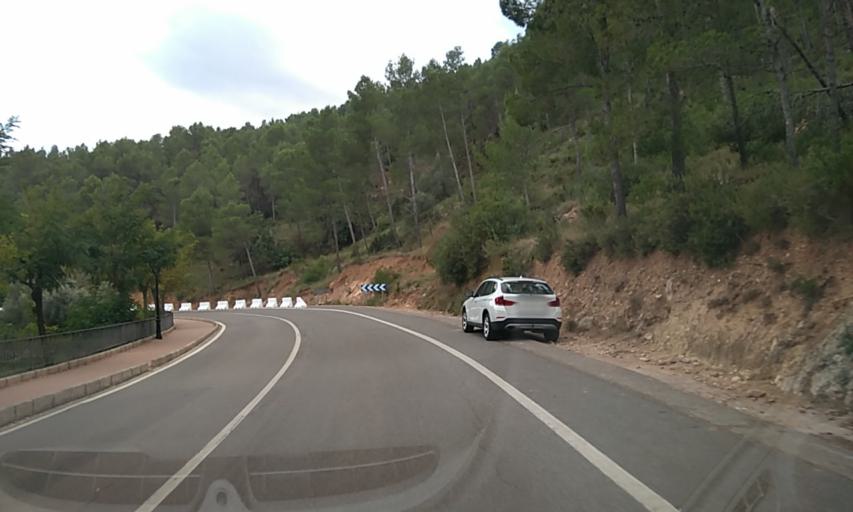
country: ES
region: Valencia
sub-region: Provincia de Castello
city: Montanejos
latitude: 40.0743
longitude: -0.5299
